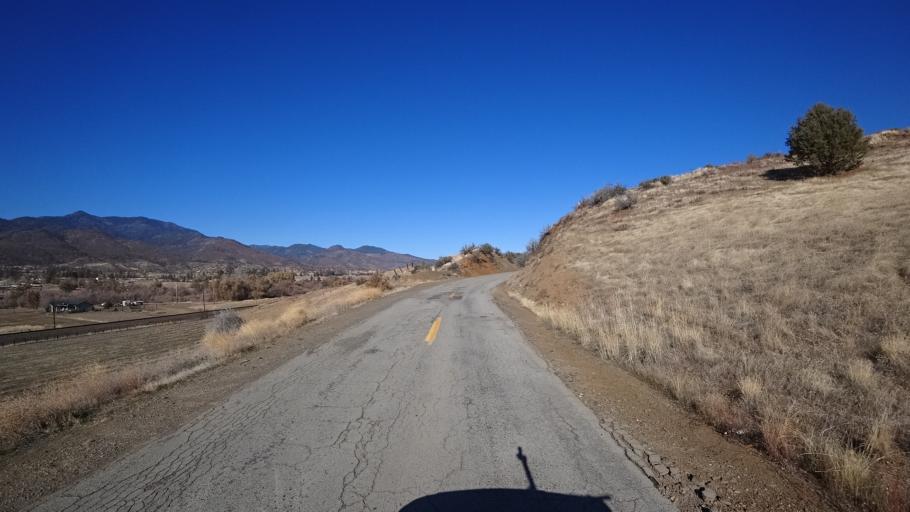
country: US
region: California
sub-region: Siskiyou County
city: Montague
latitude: 41.8996
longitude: -122.5441
